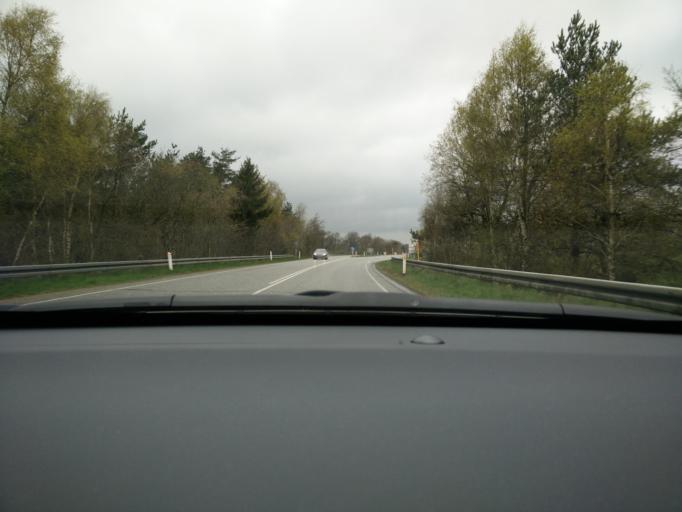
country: DK
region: Central Jutland
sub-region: Viborg Kommune
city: Viborg
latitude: 56.5050
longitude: 9.3286
